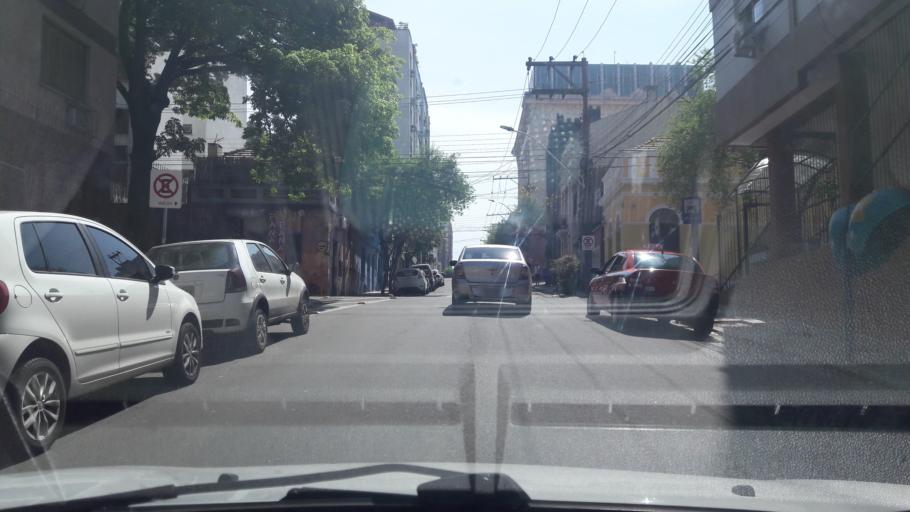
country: BR
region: Rio Grande do Sul
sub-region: Porto Alegre
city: Porto Alegre
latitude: -30.0358
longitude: -51.2376
